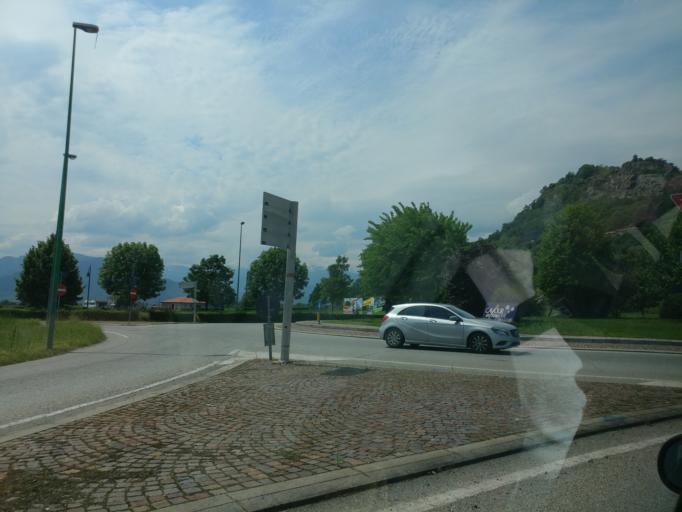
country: IT
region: Piedmont
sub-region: Provincia di Torino
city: Cavour
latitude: 44.7824
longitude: 7.3827
